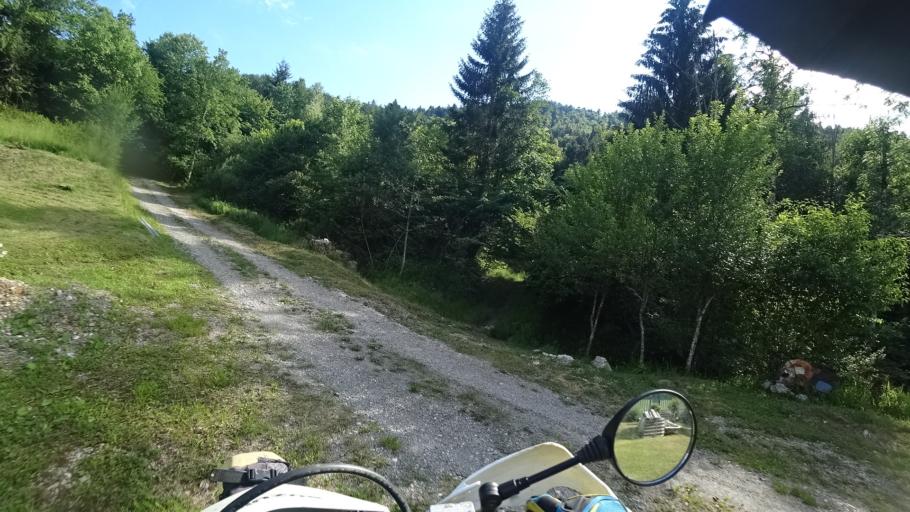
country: SI
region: Osilnica
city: Osilnica
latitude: 45.4701
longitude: 14.6967
